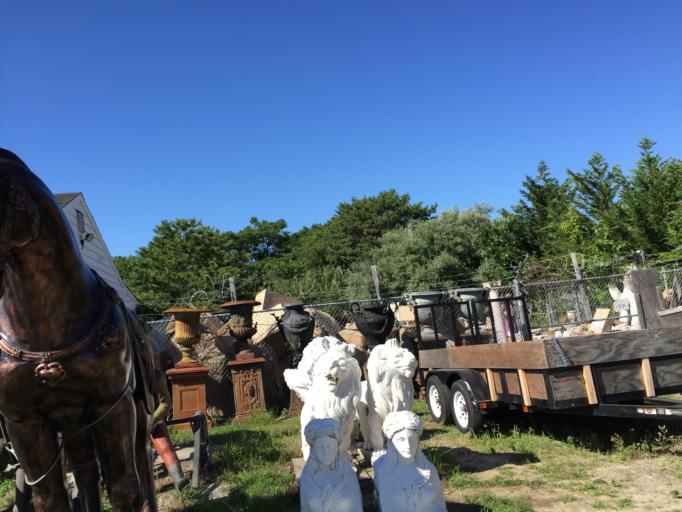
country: US
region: New York
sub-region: Suffolk County
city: Shinnecock Hills
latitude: 40.8951
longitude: -72.4502
